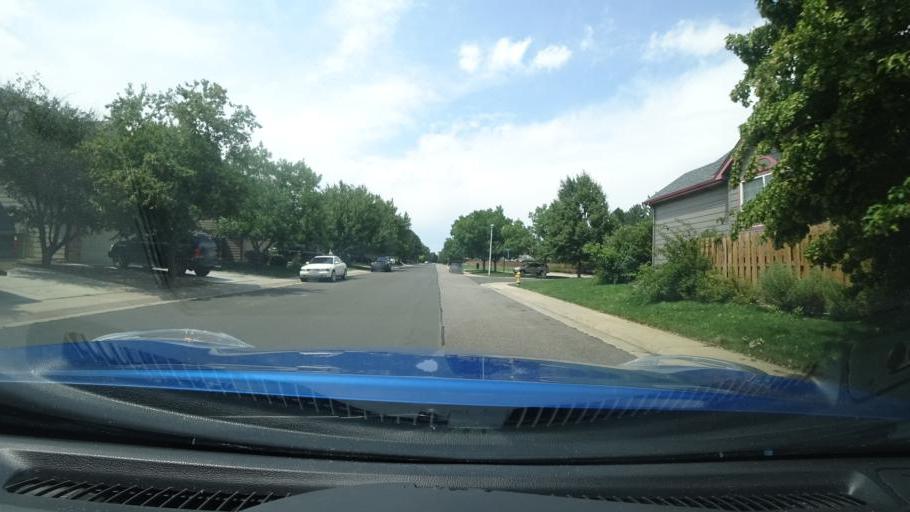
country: US
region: Colorado
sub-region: Adams County
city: Aurora
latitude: 39.6699
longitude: -104.7751
